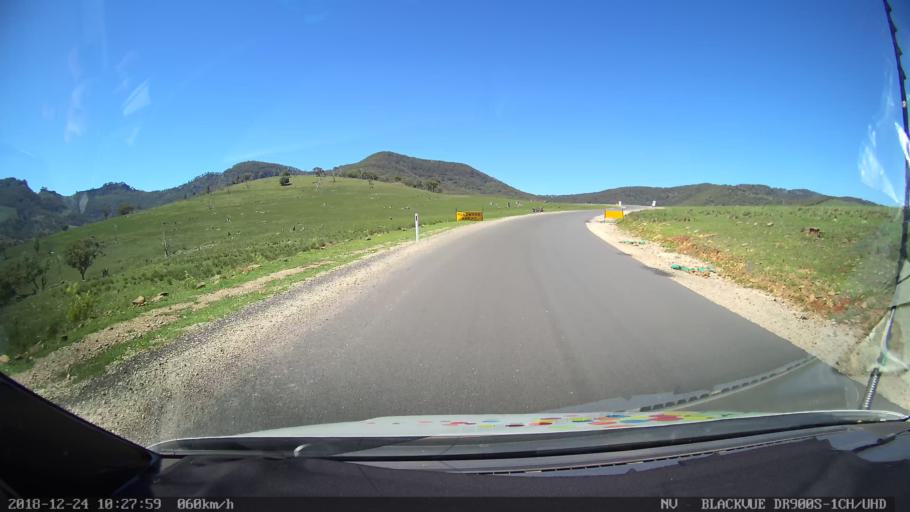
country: AU
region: New South Wales
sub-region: Liverpool Plains
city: Quirindi
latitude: -31.8233
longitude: 150.5339
